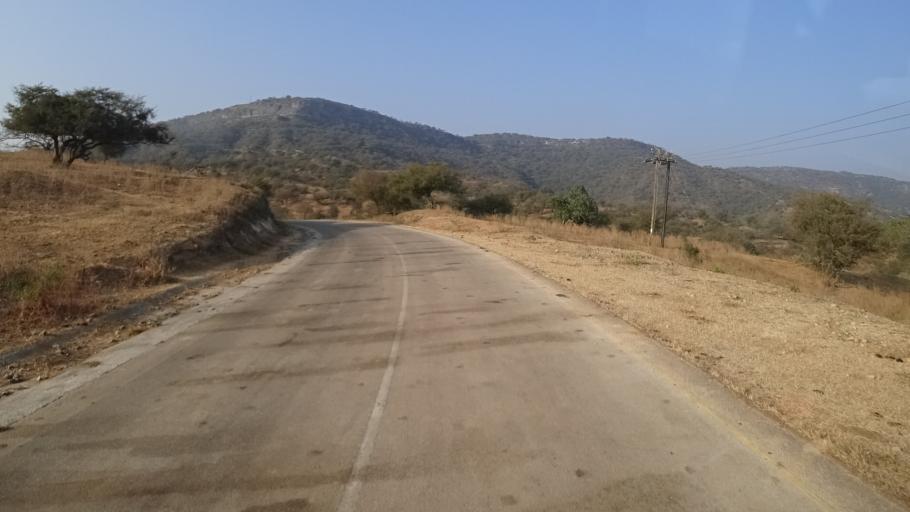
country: YE
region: Al Mahrah
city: Hawf
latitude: 16.7551
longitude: 53.3409
